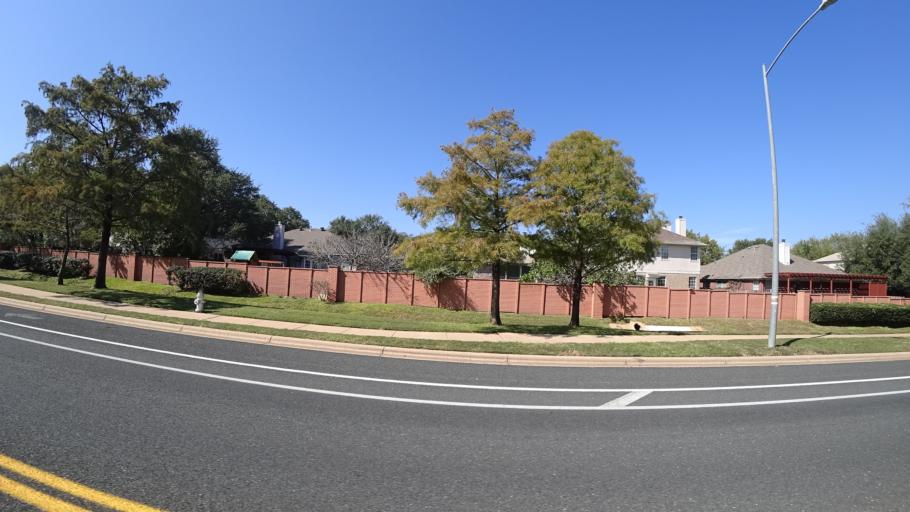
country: US
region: Texas
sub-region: Travis County
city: Shady Hollow
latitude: 30.2132
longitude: -97.8644
